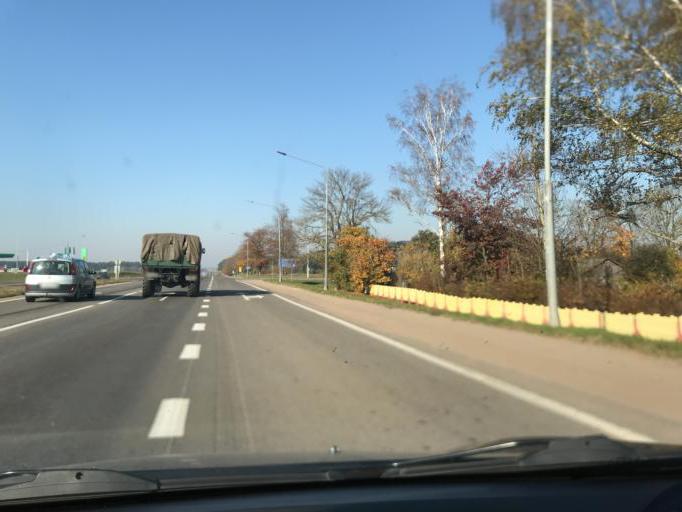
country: BY
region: Minsk
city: Dukora
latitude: 53.7044
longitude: 27.8794
